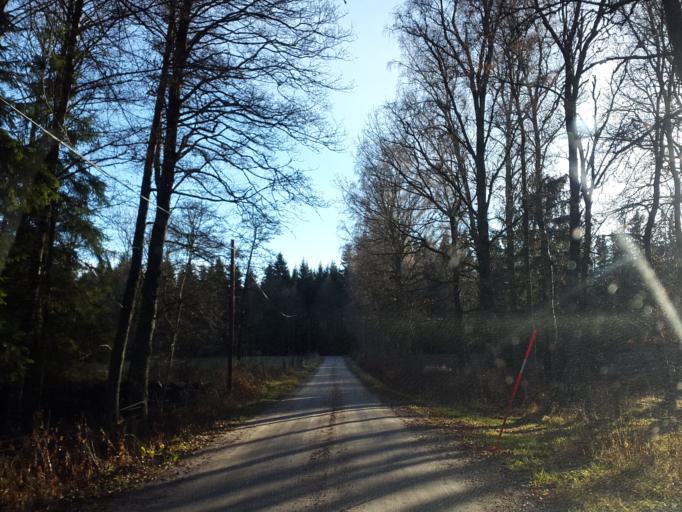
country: SE
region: Vaestra Goetaland
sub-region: Herrljunga Kommun
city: Herrljunga
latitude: 58.0599
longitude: 12.9554
